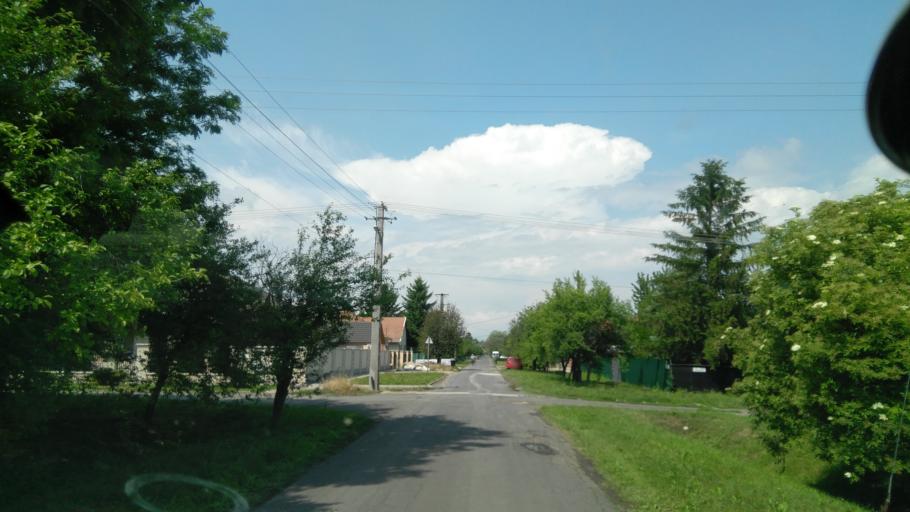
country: HU
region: Bekes
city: Bekes
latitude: 46.7579
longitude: 21.1465
